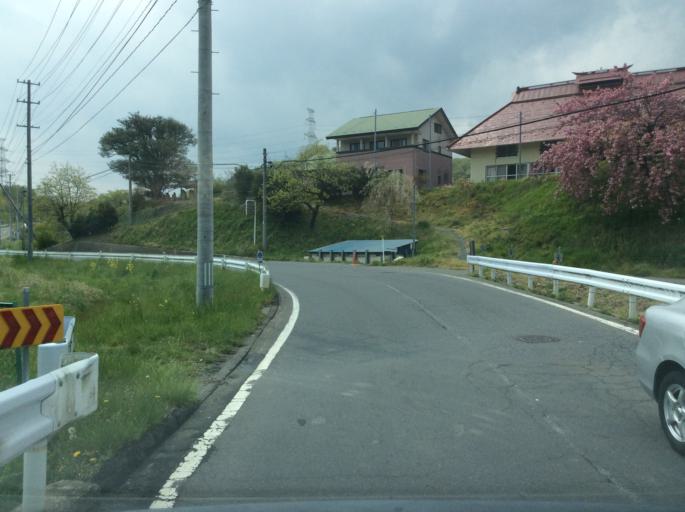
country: JP
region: Fukushima
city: Miharu
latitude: 37.3936
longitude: 140.4515
